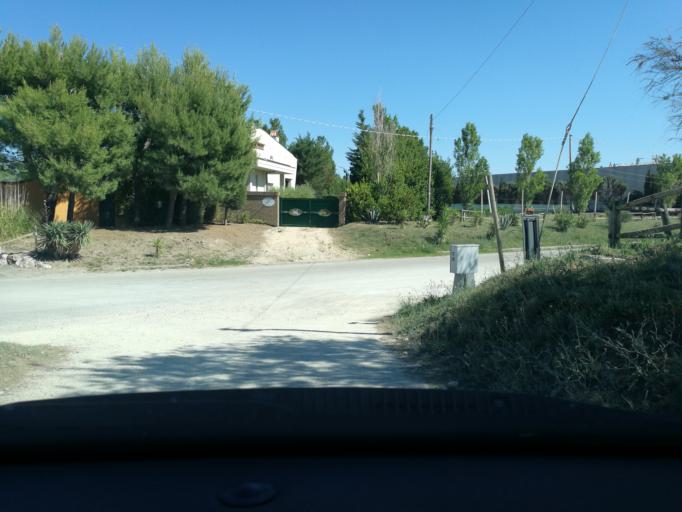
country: IT
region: Abruzzo
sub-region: Provincia di Chieti
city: Vasto
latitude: 42.1744
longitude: 14.6935
